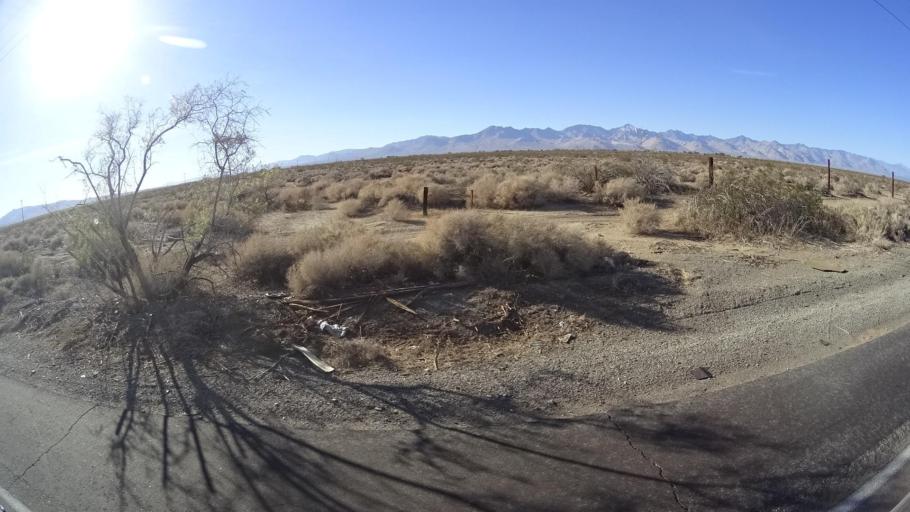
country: US
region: California
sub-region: Kern County
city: China Lake Acres
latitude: 35.6353
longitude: -117.7231
